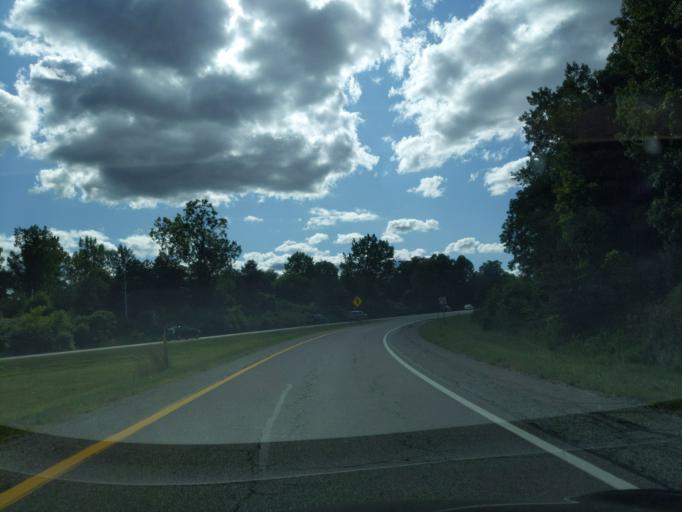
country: US
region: Michigan
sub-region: Kent County
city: Comstock Park
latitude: 43.0185
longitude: -85.6928
